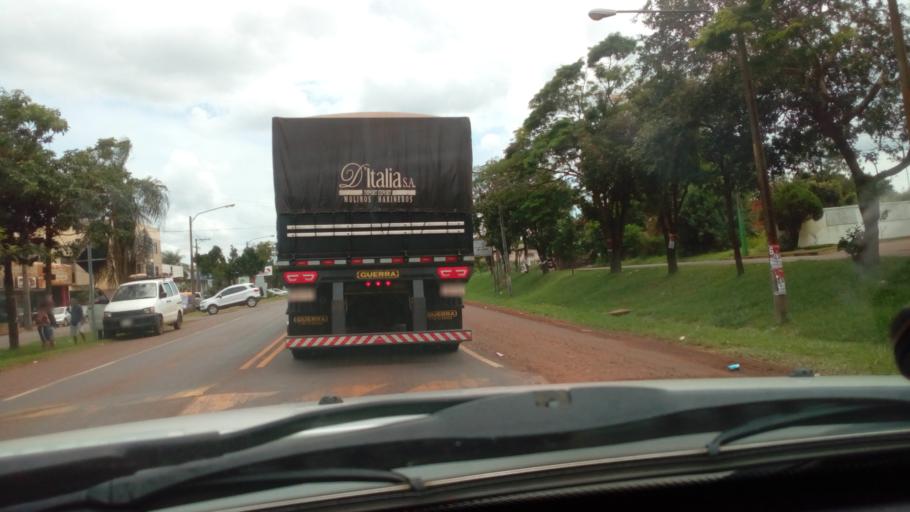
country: PY
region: Alto Parana
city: Santa Rita
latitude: -25.7855
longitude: -55.0811
